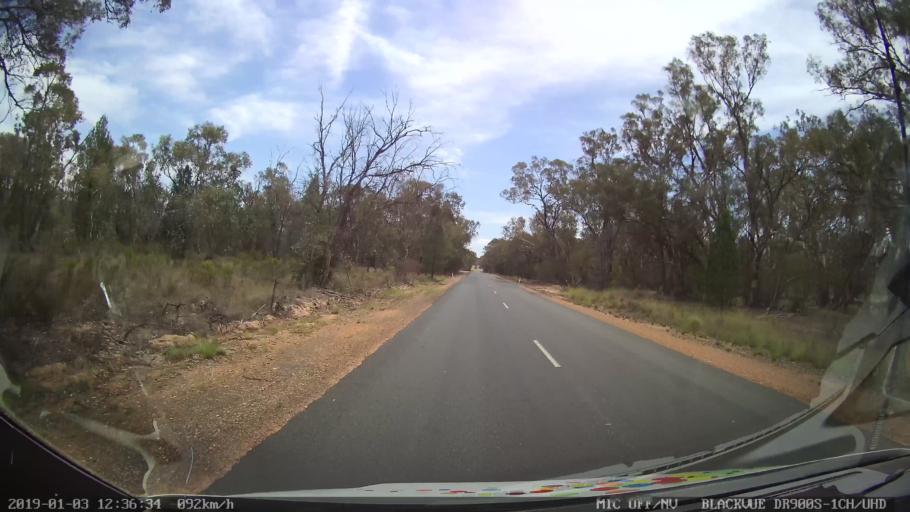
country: AU
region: New South Wales
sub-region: Weddin
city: Grenfell
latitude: -33.8532
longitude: 148.1776
